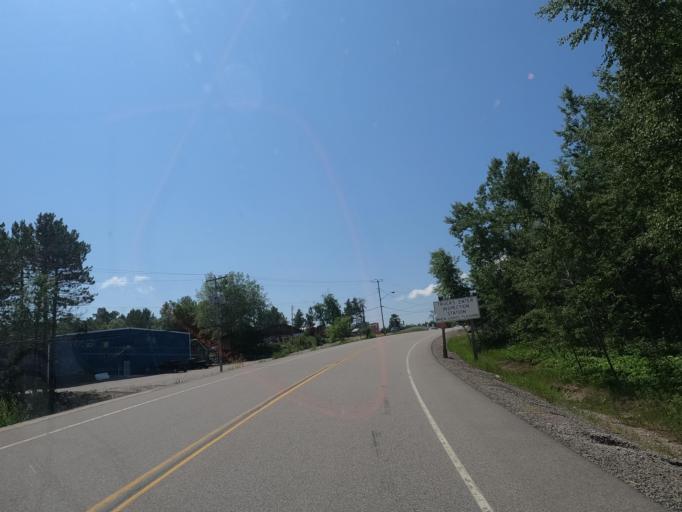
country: CA
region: Ontario
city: Dryden
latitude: 49.8549
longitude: -93.3632
